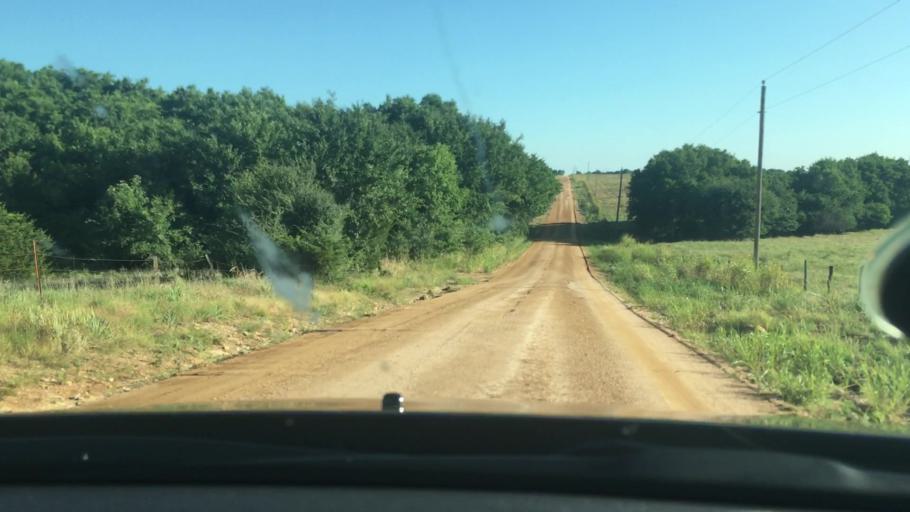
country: US
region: Oklahoma
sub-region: Murray County
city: Sulphur
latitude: 34.4108
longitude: -96.7935
